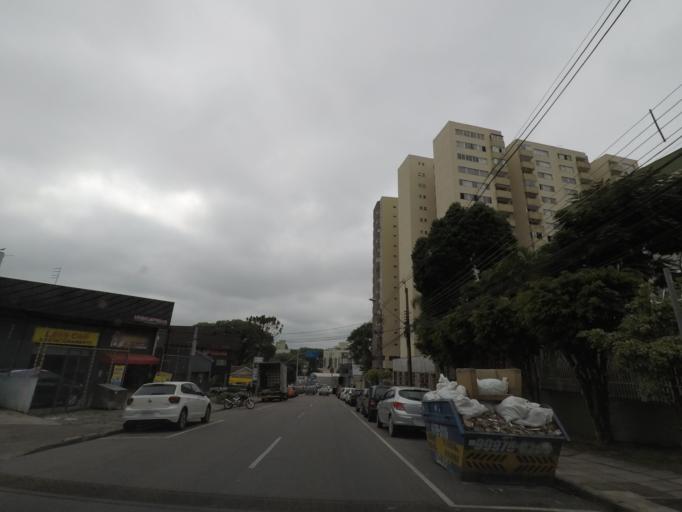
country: BR
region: Parana
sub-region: Curitiba
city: Curitiba
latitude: -25.4713
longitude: -49.2922
